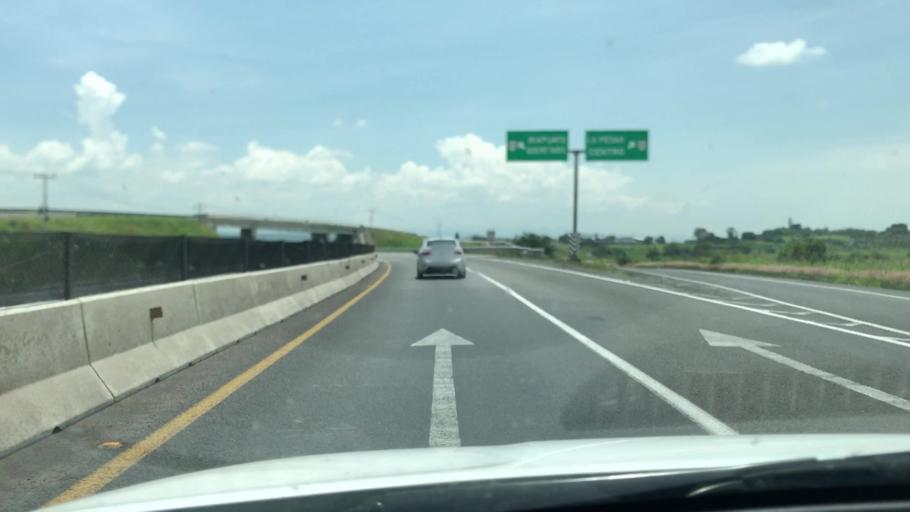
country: MX
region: Jalisco
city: Degollado
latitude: 20.3669
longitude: -102.1303
